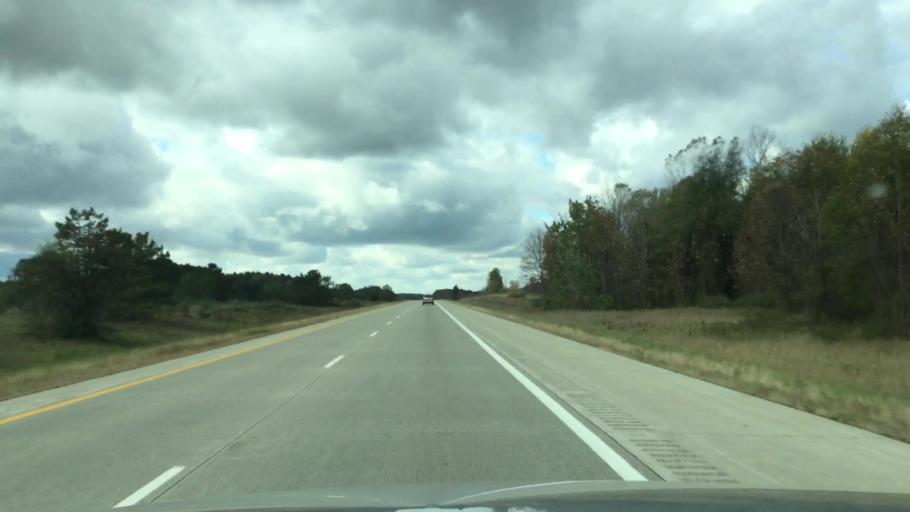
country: US
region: Michigan
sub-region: Lapeer County
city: Lapeer
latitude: 43.0269
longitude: -83.3936
